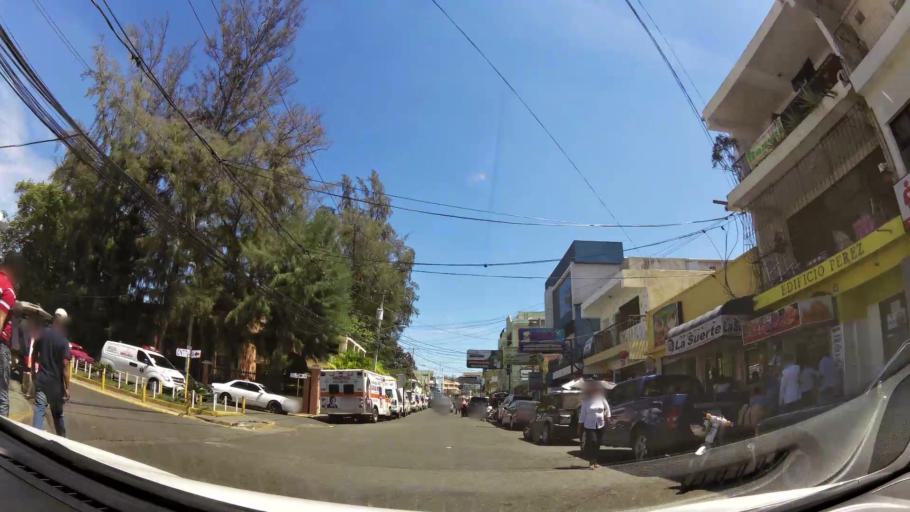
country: DO
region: Santiago
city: Santiago de los Caballeros
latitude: 19.4547
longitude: -70.7001
